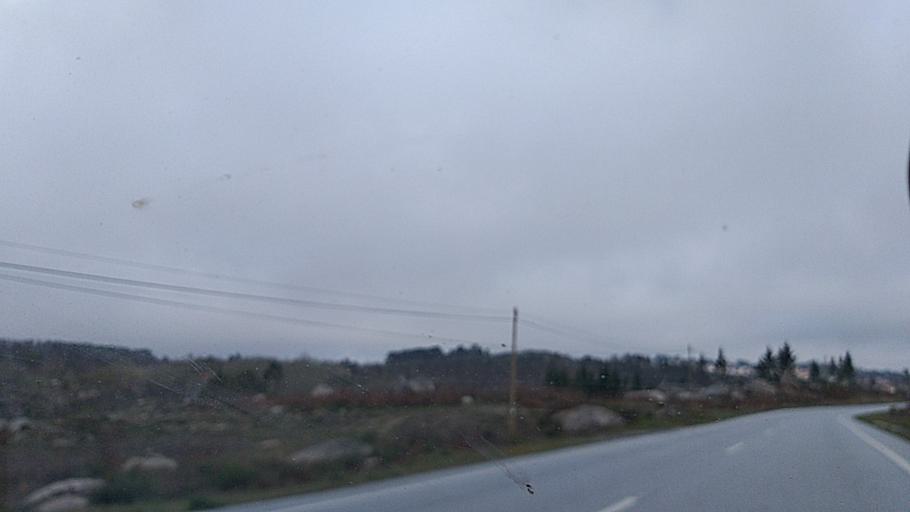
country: PT
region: Guarda
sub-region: Fornos de Algodres
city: Fornos de Algodres
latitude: 40.6727
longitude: -7.4735
